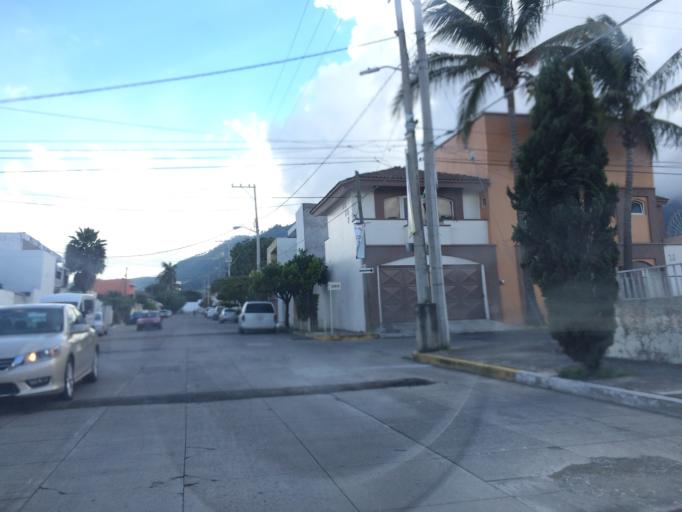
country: MX
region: Nayarit
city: Tepic
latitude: 21.5078
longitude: -104.9043
